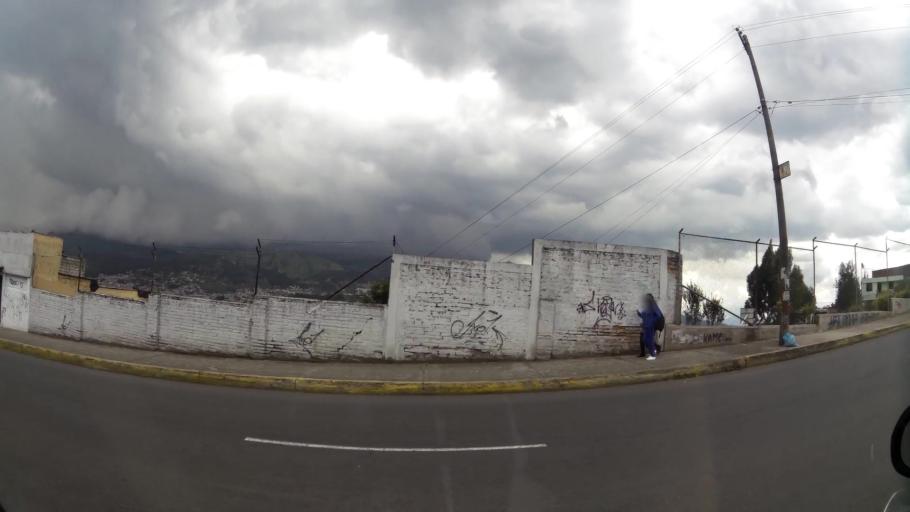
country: EC
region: Pichincha
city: Quito
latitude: -0.2457
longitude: -78.5041
